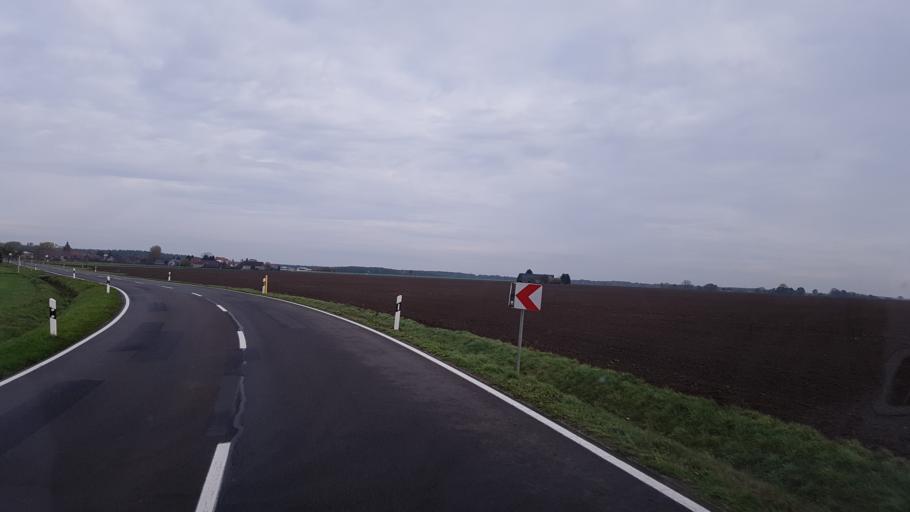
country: DE
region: Brandenburg
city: Doberlug-Kirchhain
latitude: 51.6814
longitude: 13.5119
